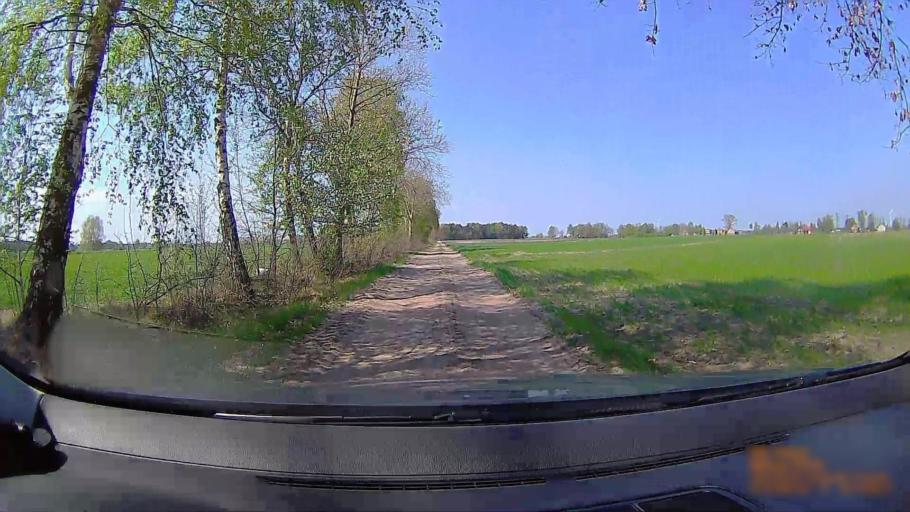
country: PL
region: Greater Poland Voivodeship
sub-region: Powiat koninski
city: Rychwal
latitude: 52.1019
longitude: 18.1815
